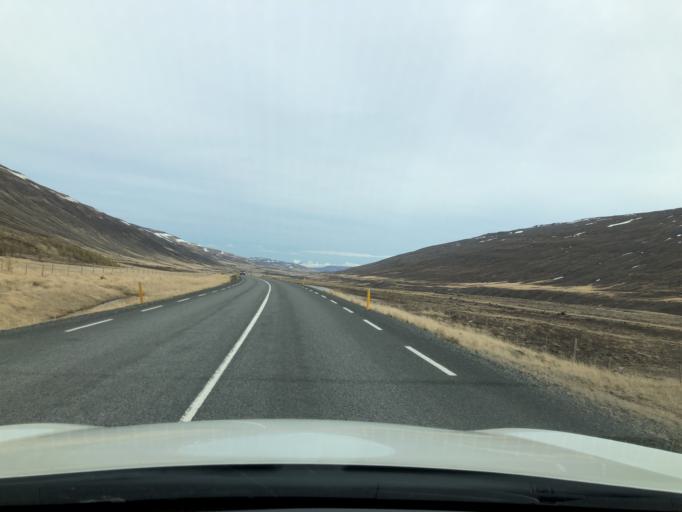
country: IS
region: East
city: Egilsstadir
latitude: 65.3311
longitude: -15.0728
